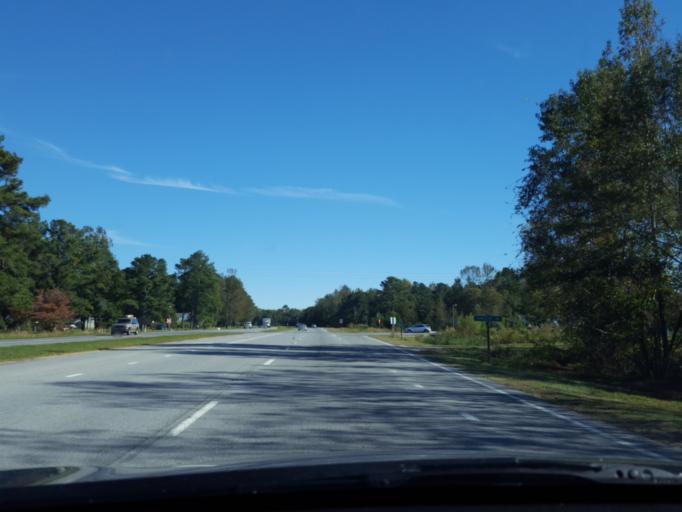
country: US
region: North Carolina
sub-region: Beaufort County
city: Washington
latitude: 35.6104
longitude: -77.1543
